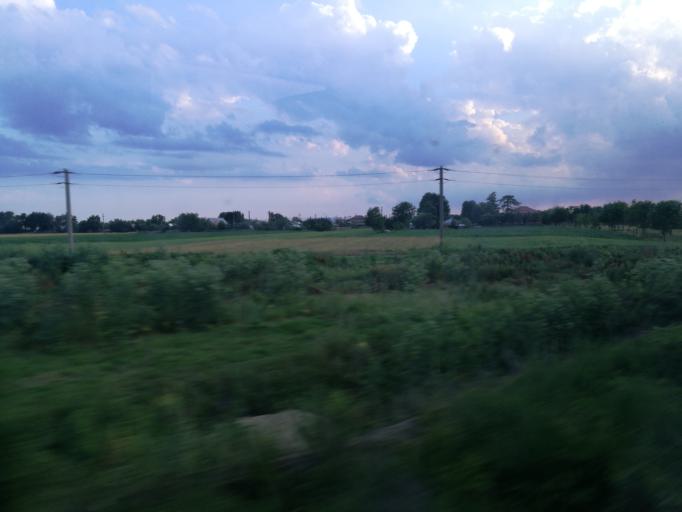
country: RO
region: Dambovita
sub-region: Comuna Titu
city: Titu
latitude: 44.6685
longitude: 25.5282
